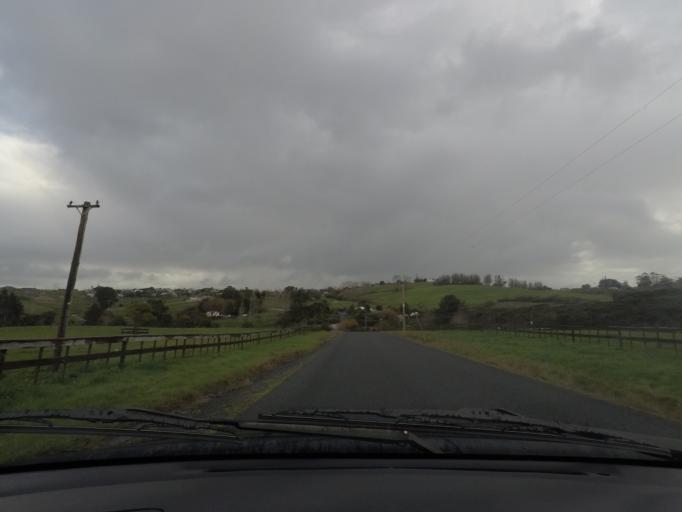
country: NZ
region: Auckland
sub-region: Auckland
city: Warkworth
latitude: -36.4344
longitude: 174.7308
